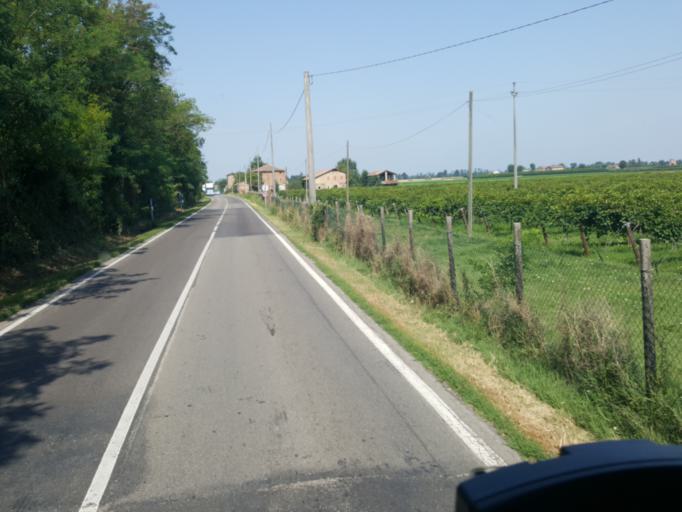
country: IT
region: Emilia-Romagna
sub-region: Provincia di Modena
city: San Vito
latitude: 44.5346
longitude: 10.9821
